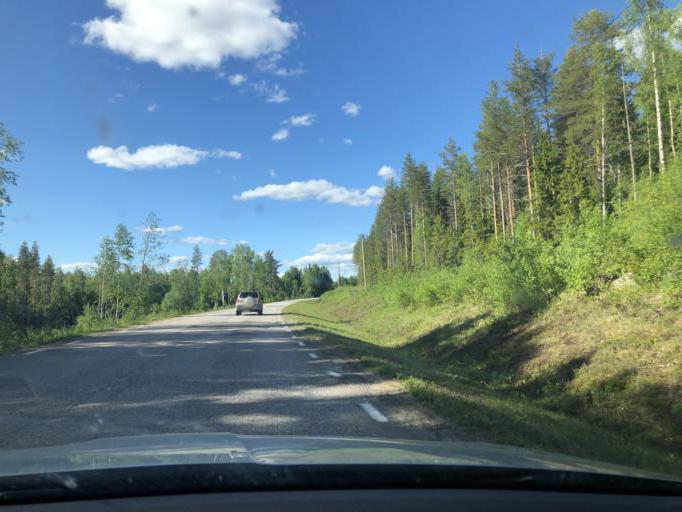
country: SE
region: Norrbotten
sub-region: Kalix Kommun
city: Kalix
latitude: 65.9420
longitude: 23.1536
